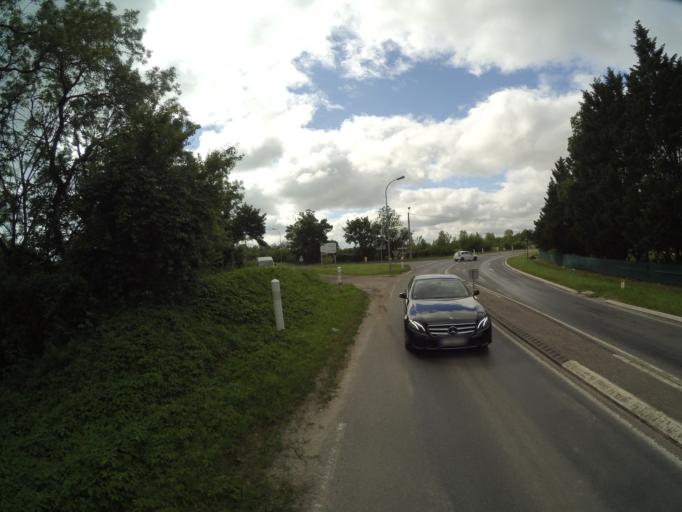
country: FR
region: Aquitaine
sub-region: Departement de la Gironde
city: Ludon-Medoc
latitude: 44.9856
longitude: -0.5764
